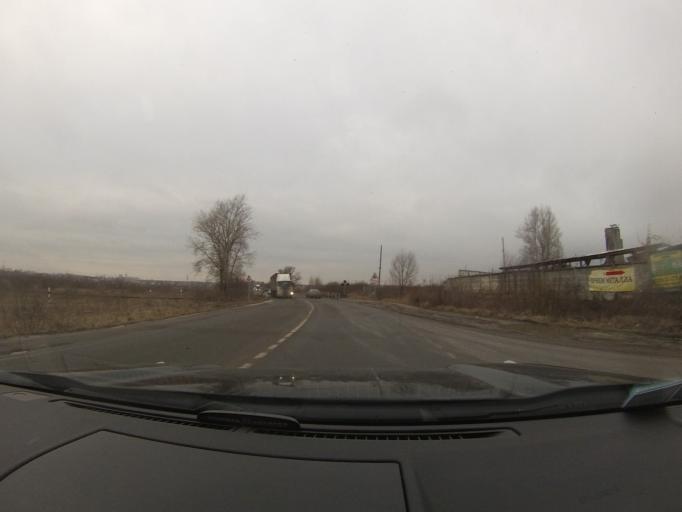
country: RU
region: Moskovskaya
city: Lopatinskiy
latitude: 55.3259
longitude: 38.7349
